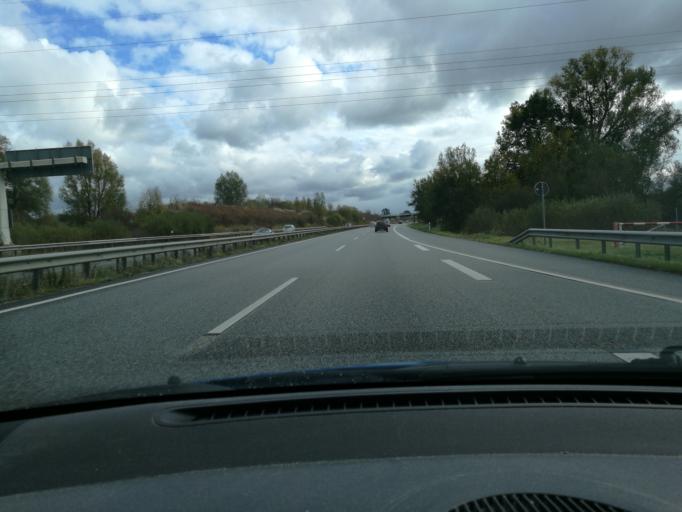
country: DE
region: Schleswig-Holstein
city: Krummesse
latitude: 53.8288
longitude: 10.6494
